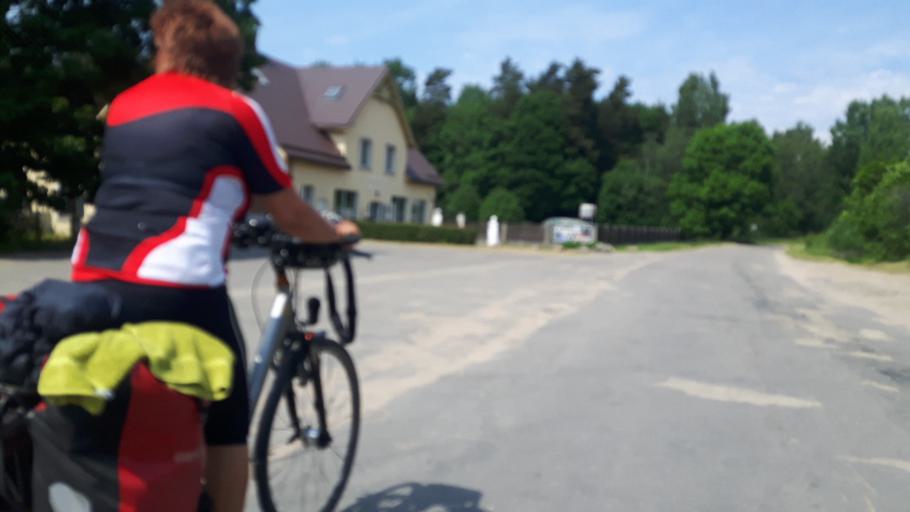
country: LV
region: Saulkrastu
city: Saulkrasti
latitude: 57.4077
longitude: 24.4236
